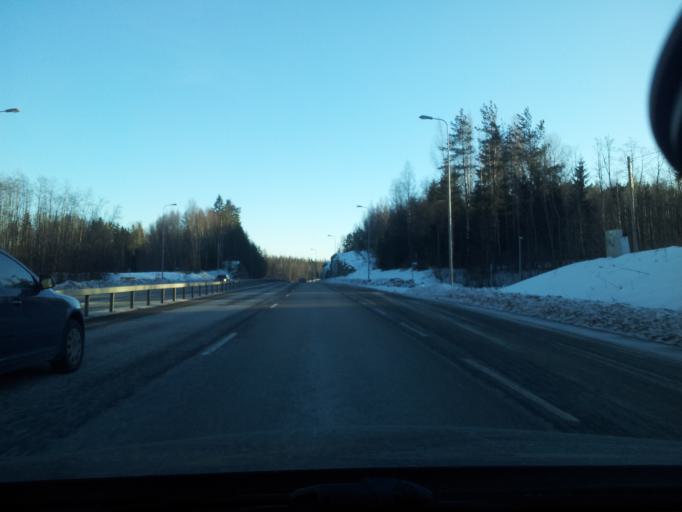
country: FI
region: Uusimaa
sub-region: Helsinki
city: Vihti
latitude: 60.3235
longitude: 24.3388
